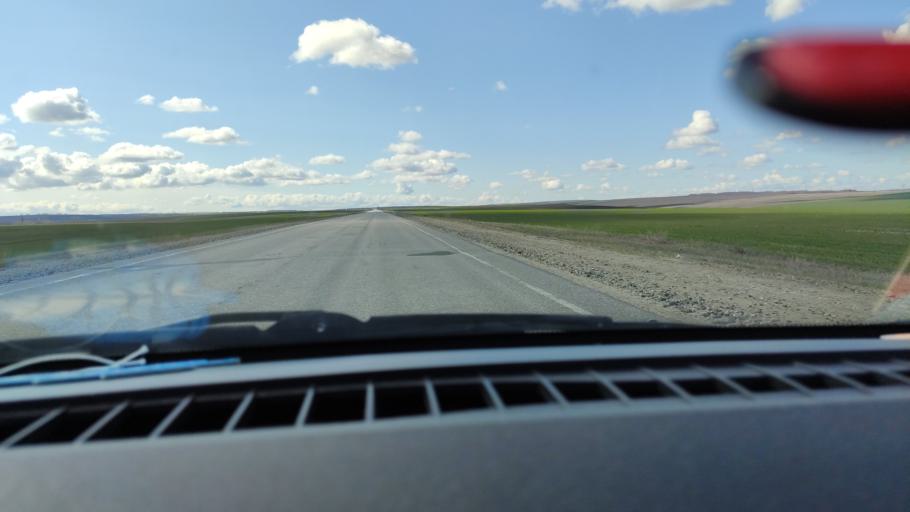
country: RU
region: Samara
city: Varlamovo
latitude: 53.0466
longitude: 48.3426
